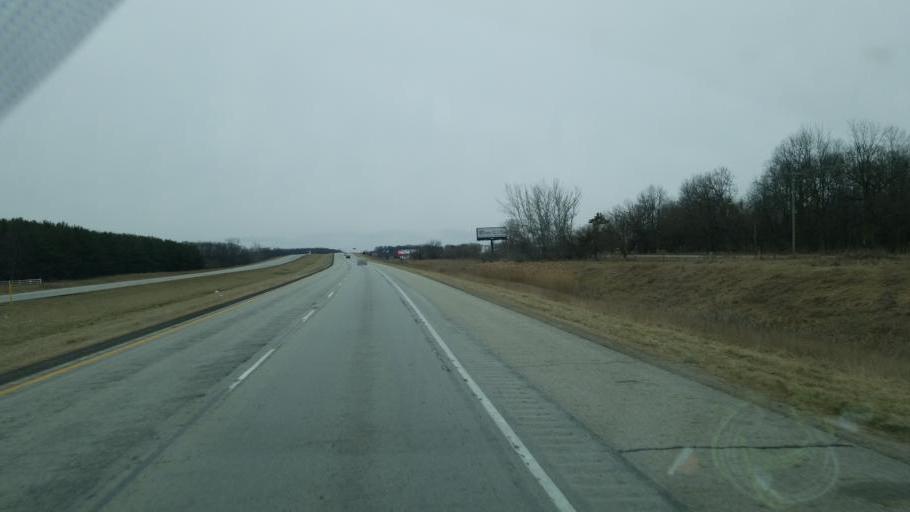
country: US
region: Indiana
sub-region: Fulton County
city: Rochester
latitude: 41.0846
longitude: -86.2412
